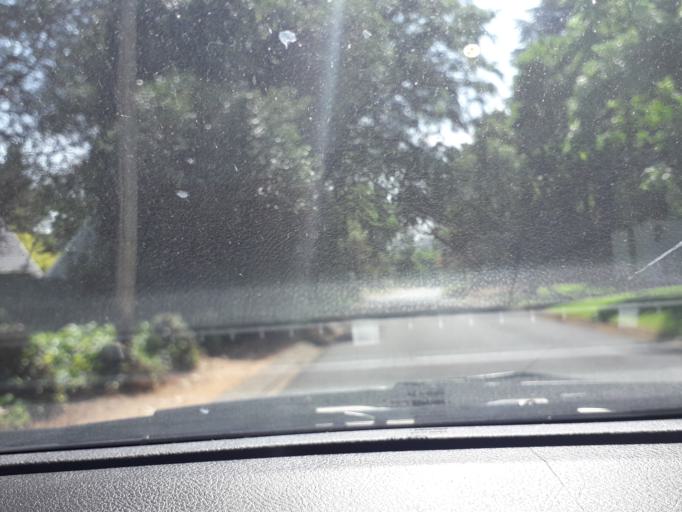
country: ZA
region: Gauteng
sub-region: City of Johannesburg Metropolitan Municipality
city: Johannesburg
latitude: -26.1207
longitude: 28.0659
